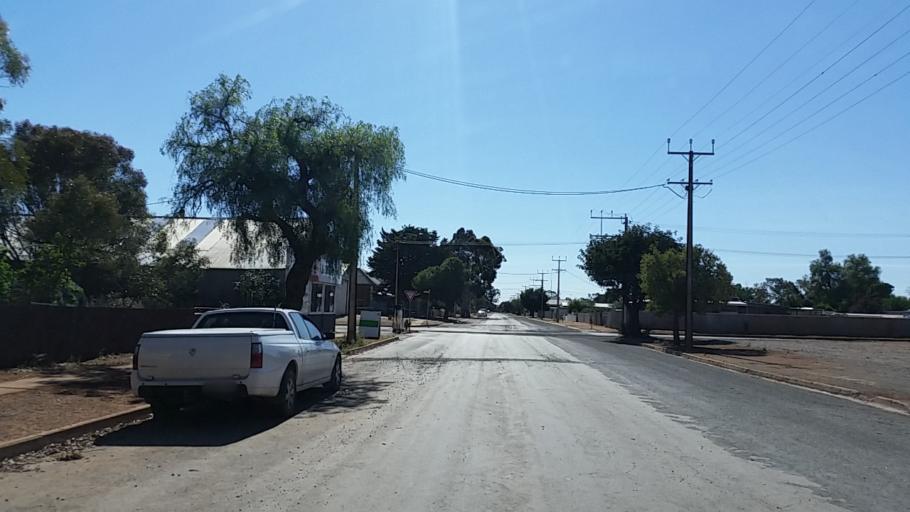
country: AU
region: South Australia
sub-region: Peterborough
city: Peterborough
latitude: -32.9721
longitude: 138.8387
